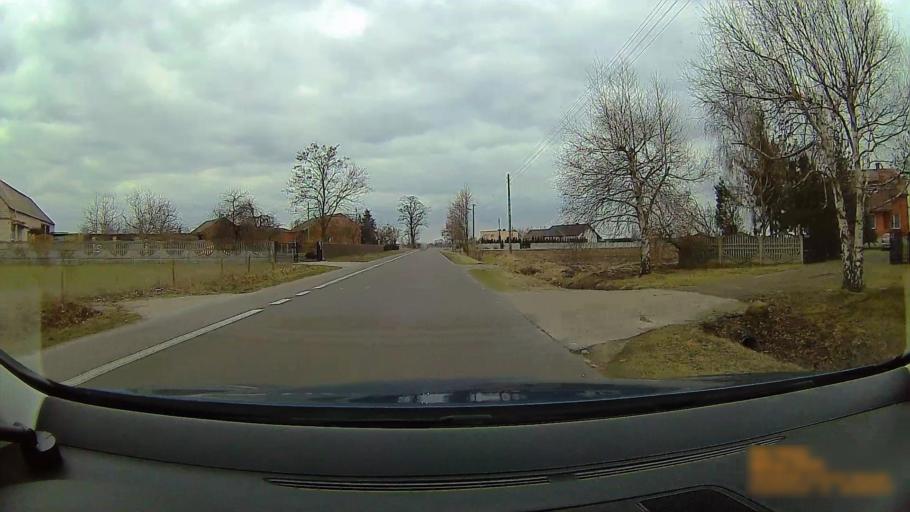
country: PL
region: Greater Poland Voivodeship
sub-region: Powiat koninski
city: Rzgow Pierwszy
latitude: 52.1183
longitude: 18.0704
